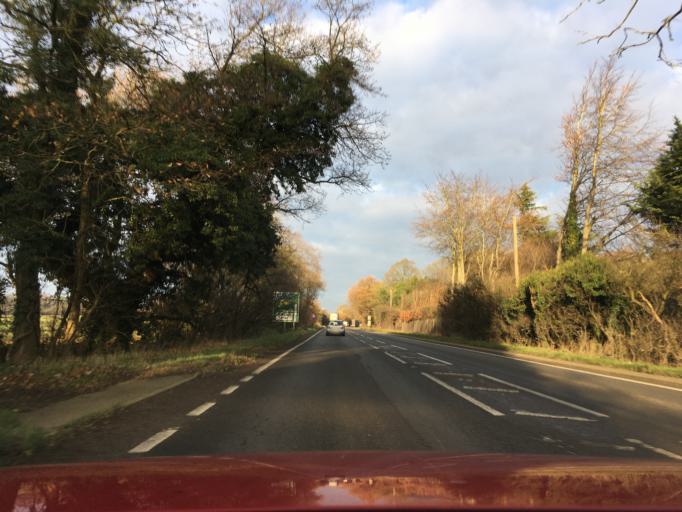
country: GB
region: England
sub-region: City and Borough of Birmingham
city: Sutton Coldfield
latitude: 52.5764
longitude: -1.7705
